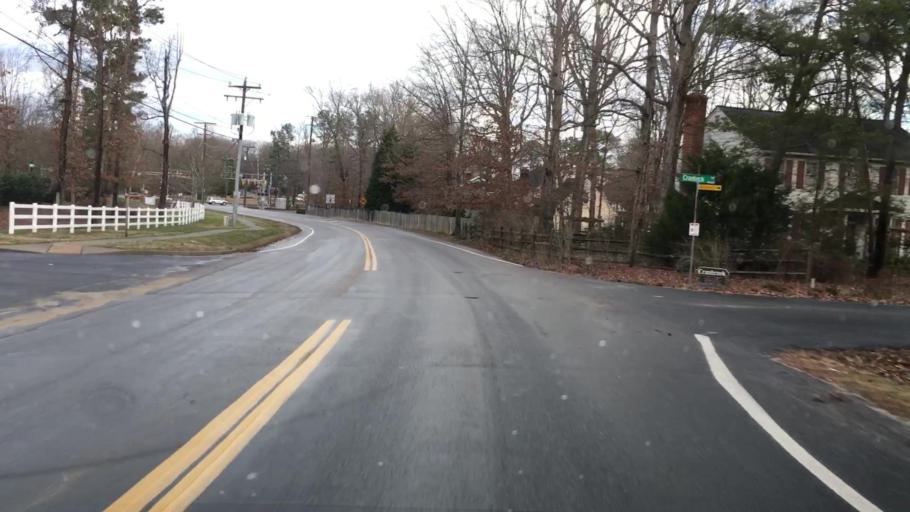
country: US
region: Virginia
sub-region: Chesterfield County
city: Bon Air
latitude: 37.5231
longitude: -77.6034
